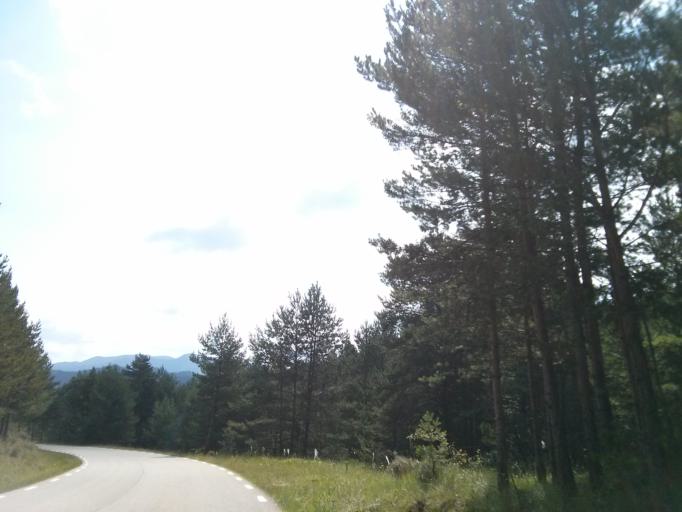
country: ES
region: Catalonia
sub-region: Provincia de Barcelona
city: Borreda
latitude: 42.1849
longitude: 2.0147
